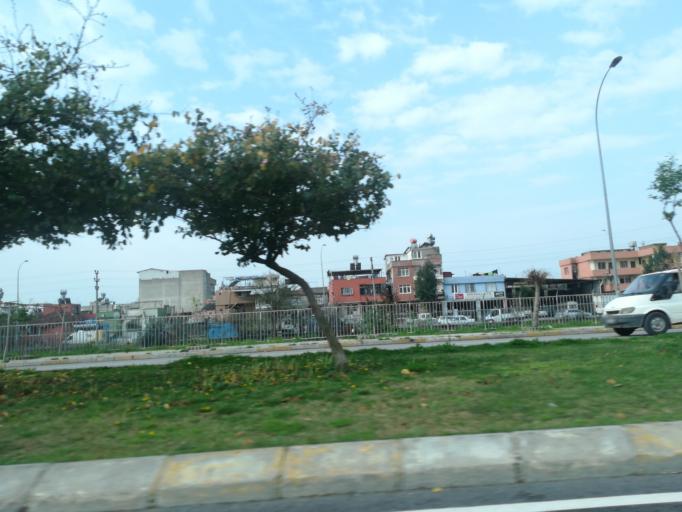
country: TR
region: Adana
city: Yuregir
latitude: 36.9963
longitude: 35.3589
